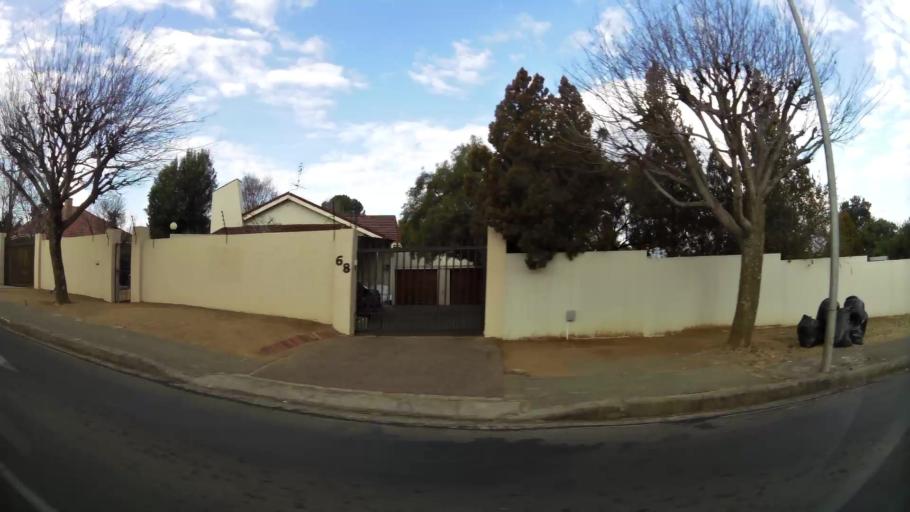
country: ZA
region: Orange Free State
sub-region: Mangaung Metropolitan Municipality
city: Bloemfontein
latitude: -29.0884
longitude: 26.2045
